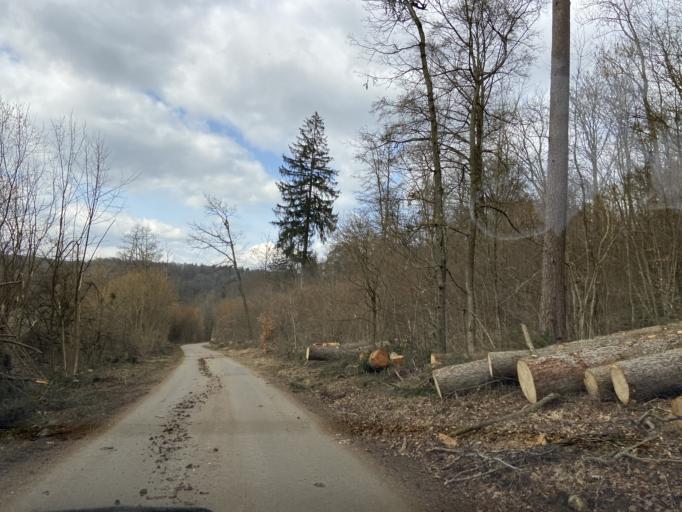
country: DE
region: Baden-Wuerttemberg
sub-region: Tuebingen Region
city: Bingen
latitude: 48.1202
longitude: 9.2628
